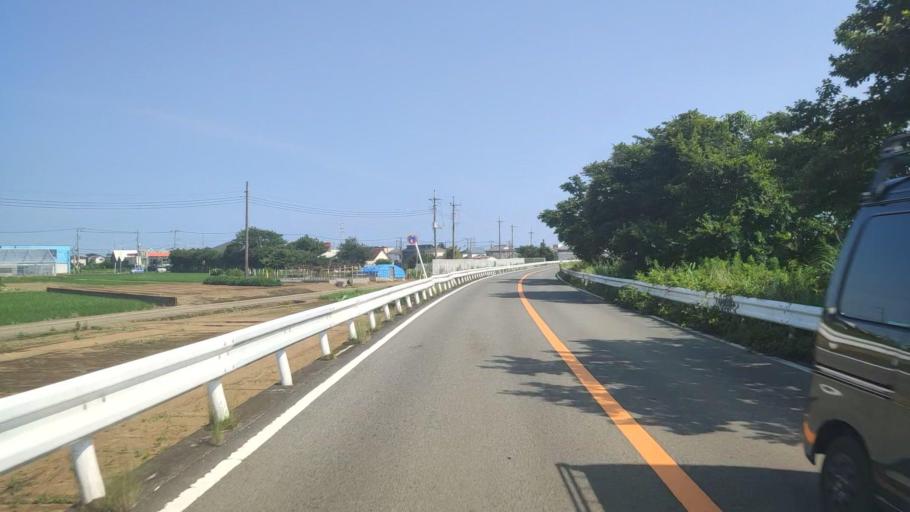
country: JP
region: Kanagawa
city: Isehara
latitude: 35.3627
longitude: 139.3227
